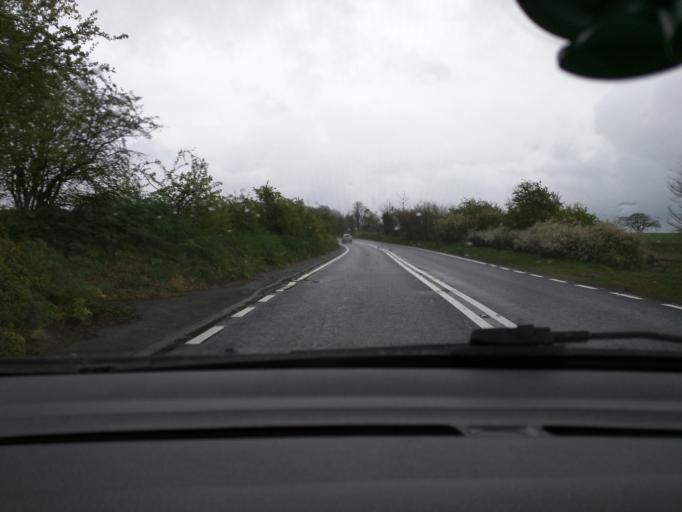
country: GB
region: England
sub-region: Suffolk
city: Wickham Market
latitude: 52.1703
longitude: 1.4090
